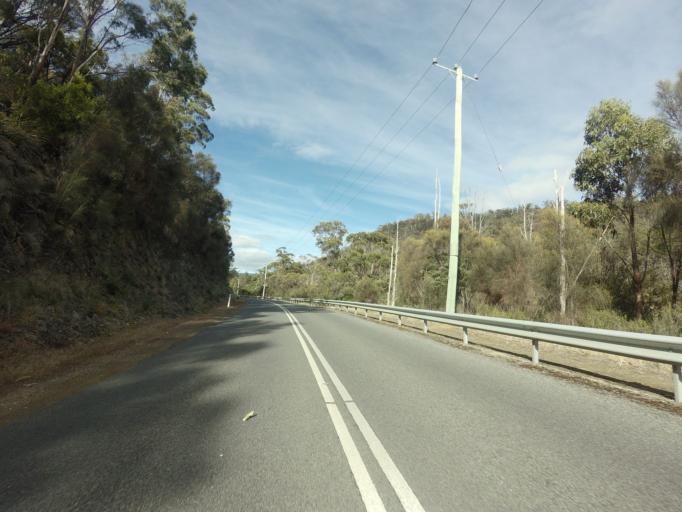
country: AU
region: Tasmania
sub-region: Clarence
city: Sandford
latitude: -43.1110
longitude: 147.7470
